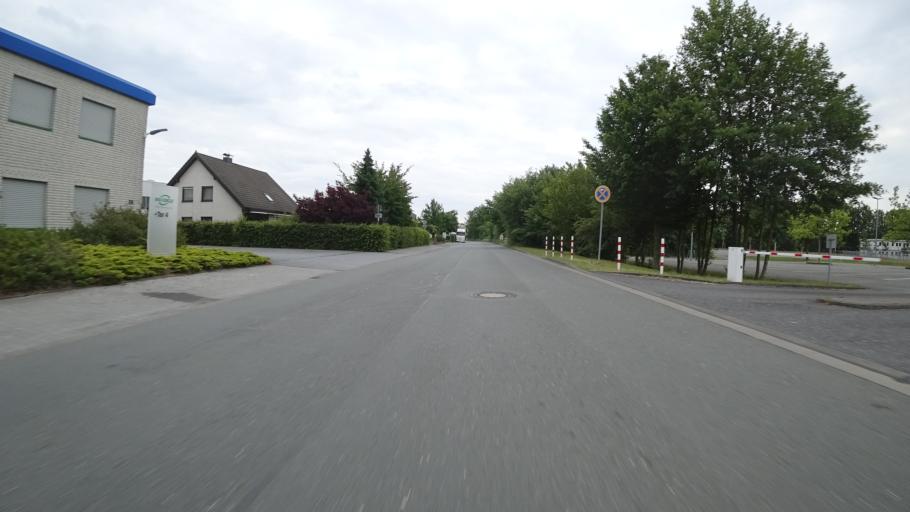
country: DE
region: North Rhine-Westphalia
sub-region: Regierungsbezirk Detmold
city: Verl
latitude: 51.8849
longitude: 8.4486
